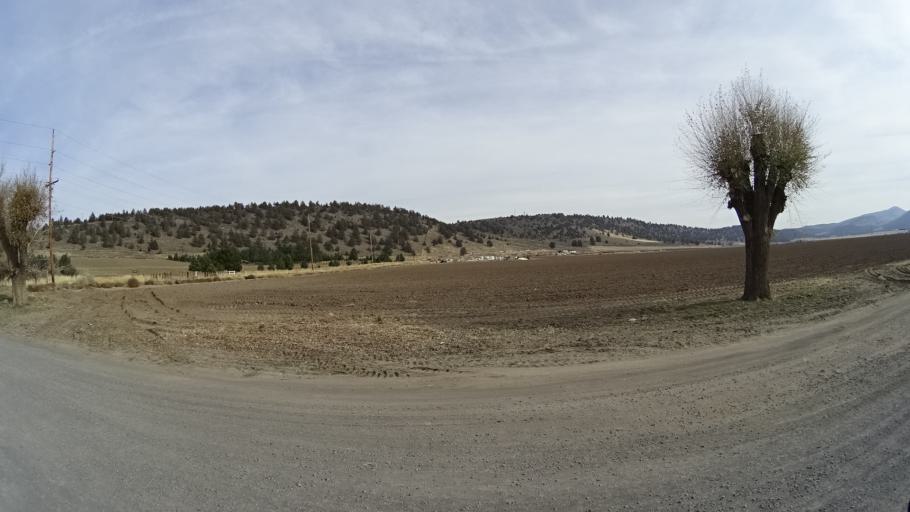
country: US
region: Oregon
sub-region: Klamath County
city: Klamath Falls
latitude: 41.9665
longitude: -121.9115
